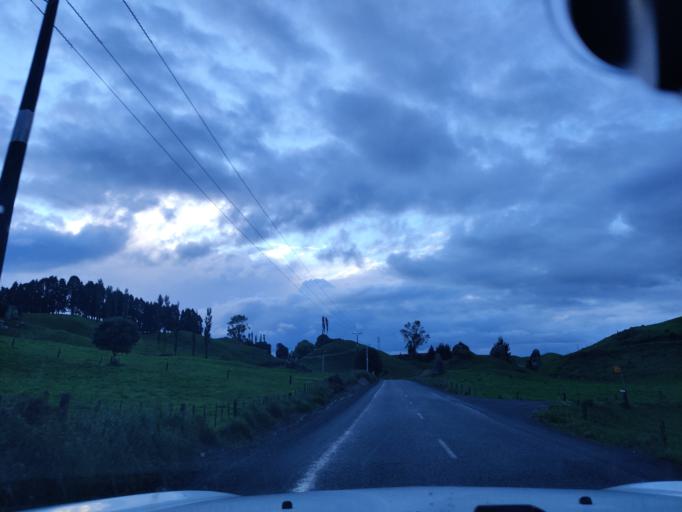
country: NZ
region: Waikato
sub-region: South Waikato District
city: Tokoroa
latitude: -38.2002
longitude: 175.8099
